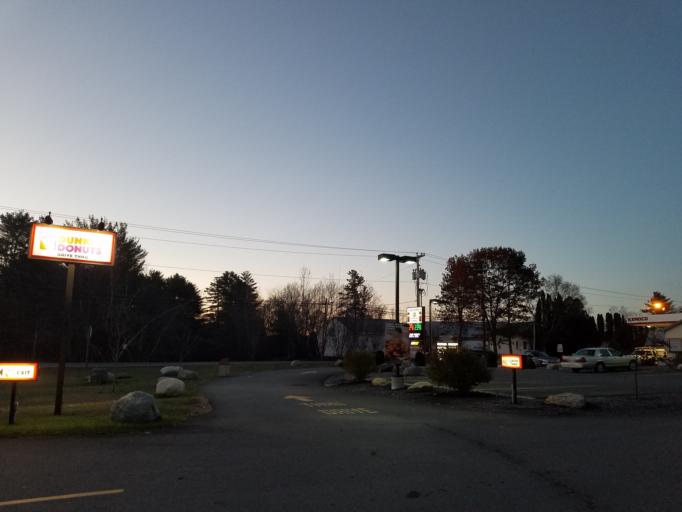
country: US
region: Maine
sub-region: Waldo County
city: Troy
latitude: 44.6168
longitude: -69.3180
